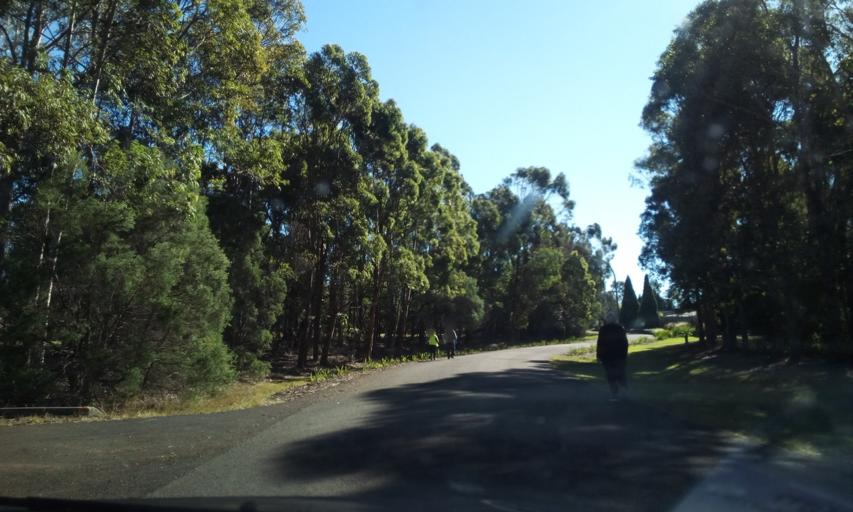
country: AU
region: New South Wales
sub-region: Wollongong
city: Dapto
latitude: -34.5226
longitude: 150.7714
